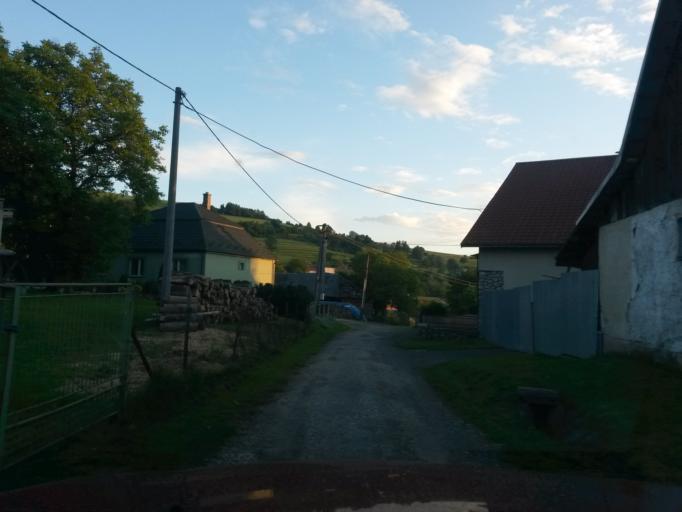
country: UA
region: Zakarpattia
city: Velykyi Bereznyi
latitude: 48.8248
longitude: 22.3580
